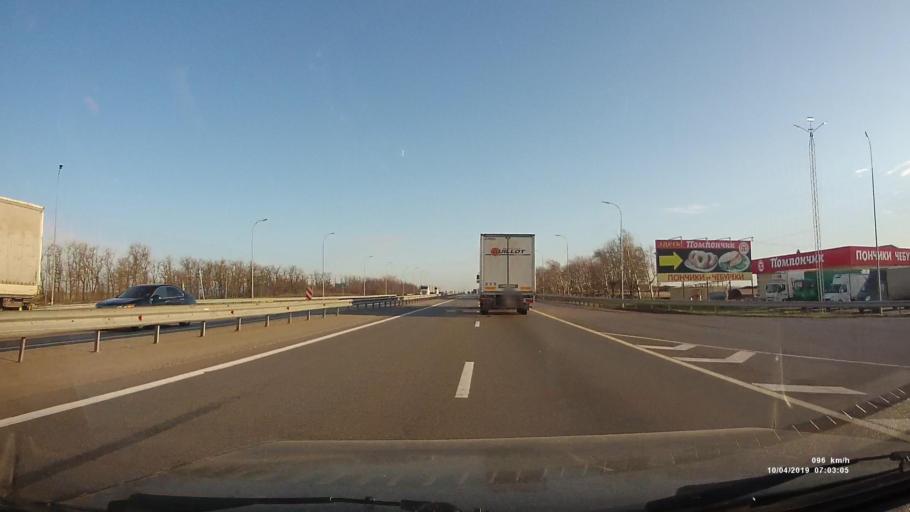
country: RU
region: Rostov
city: Krasyukovskaya
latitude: 47.6172
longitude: 39.9947
